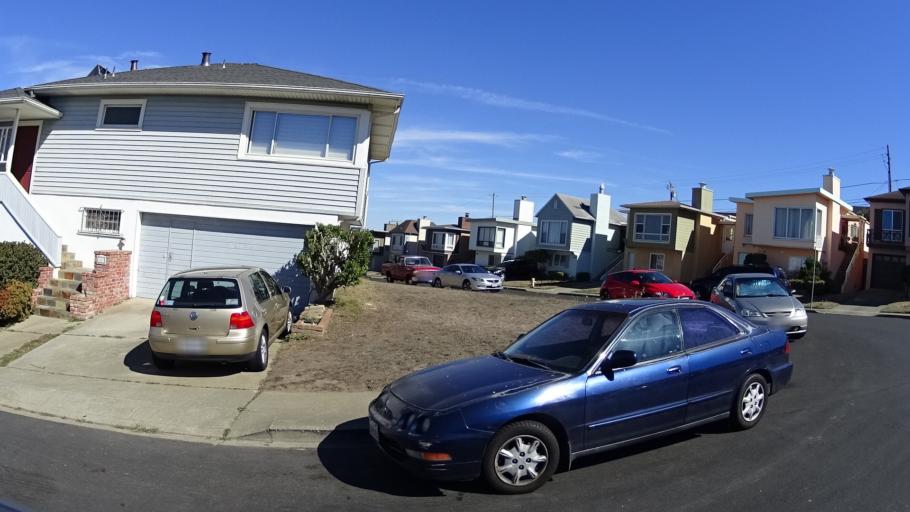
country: US
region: California
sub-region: San Mateo County
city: Broadmoor
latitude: 37.6875
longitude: -122.4945
